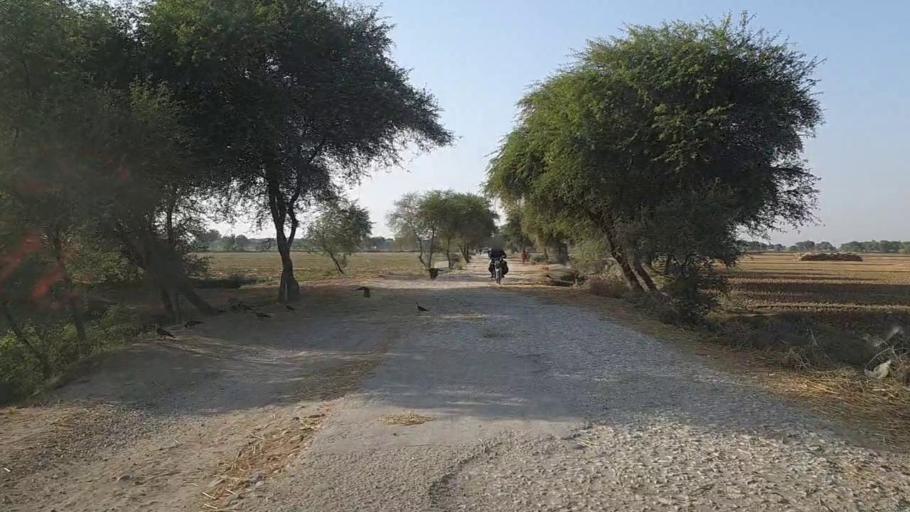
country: PK
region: Sindh
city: Kashmor
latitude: 28.4031
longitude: 69.4177
